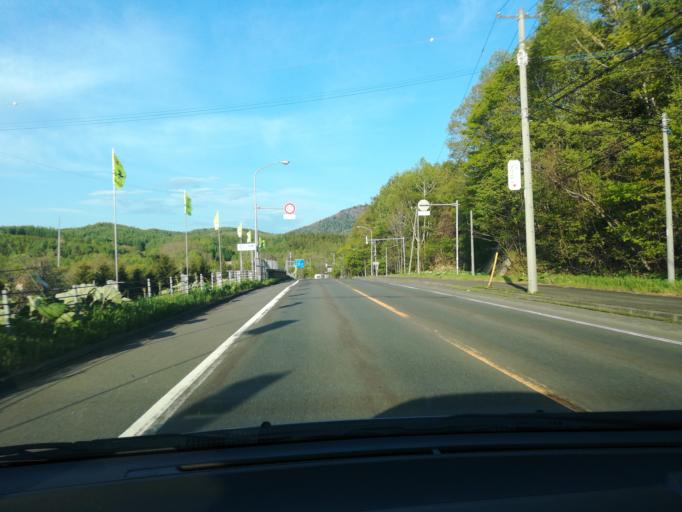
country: JP
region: Hokkaido
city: Shimo-furano
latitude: 43.1236
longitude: 142.6714
